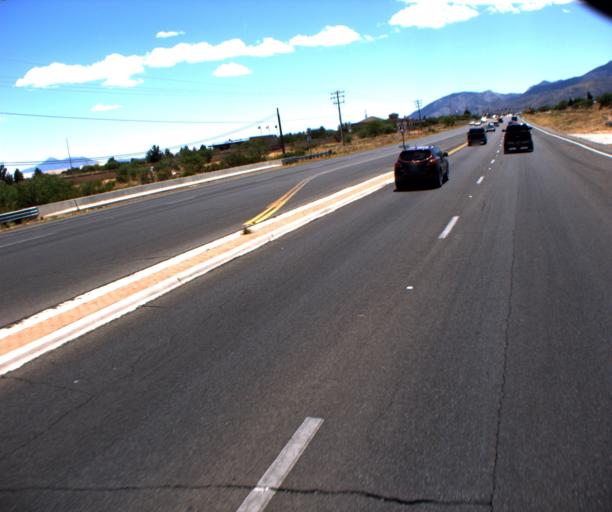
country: US
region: Arizona
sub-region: Cochise County
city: Sierra Vista
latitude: 31.5095
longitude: -110.2575
